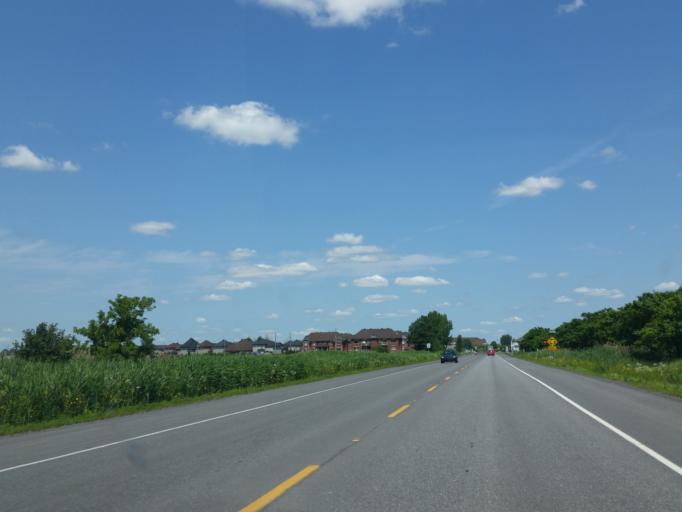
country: CA
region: Quebec
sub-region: Monteregie
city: Carignan
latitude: 45.4224
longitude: -73.3119
